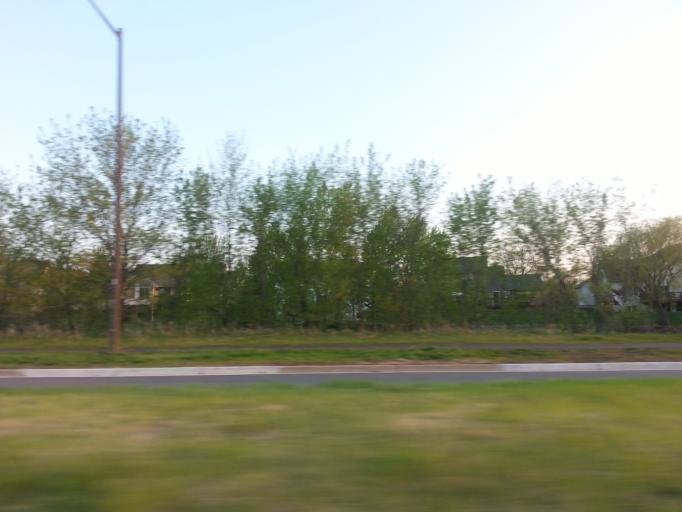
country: US
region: Minnesota
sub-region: Scott County
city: Prior Lake
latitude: 44.7393
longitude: -93.4370
